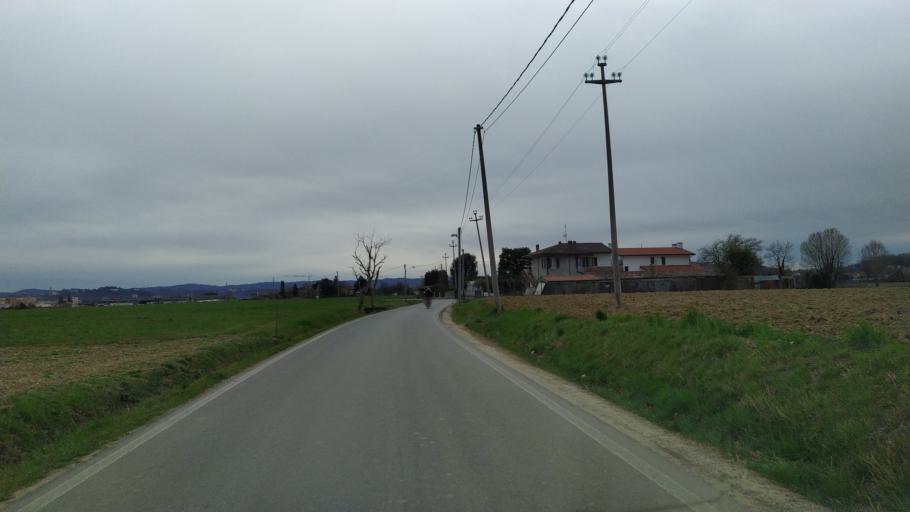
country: IT
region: Veneto
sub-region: Provincia di Vicenza
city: Crispi Cavour
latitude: 45.5820
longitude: 11.5174
